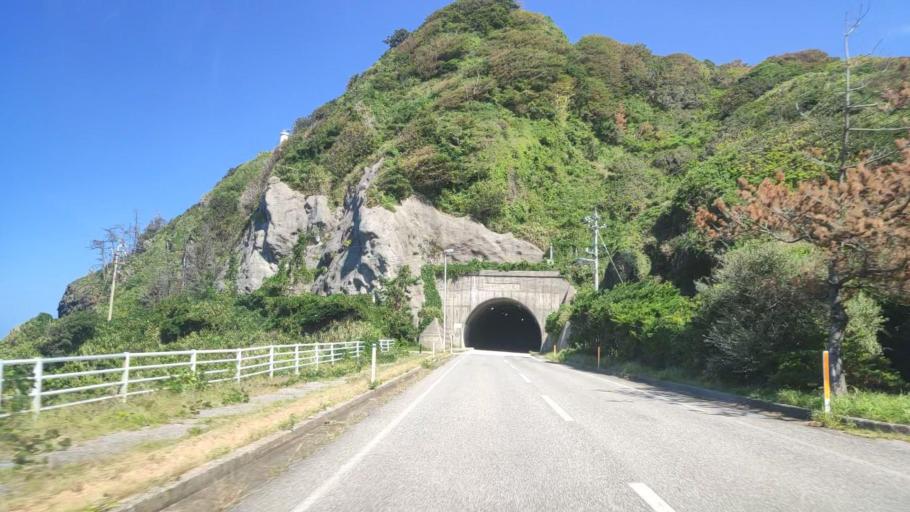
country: JP
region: Ishikawa
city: Nanao
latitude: 37.4970
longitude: 137.1437
